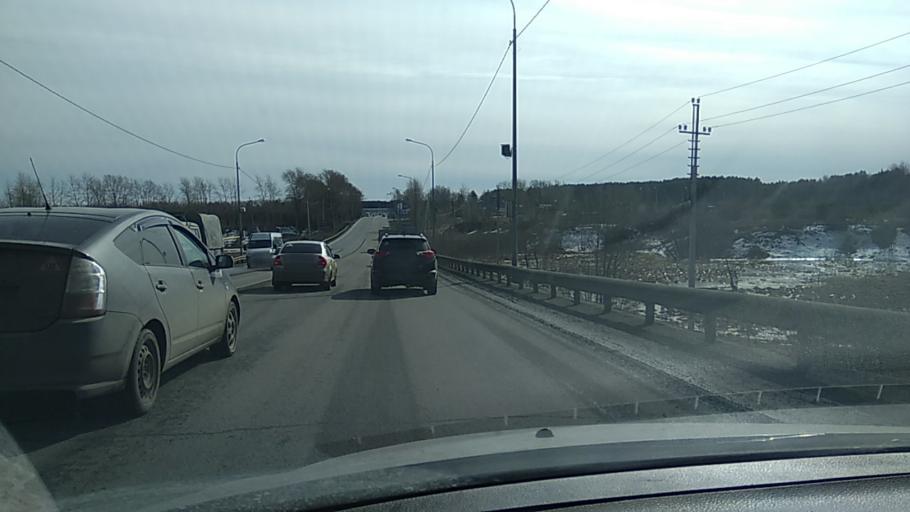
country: RU
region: Sverdlovsk
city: Nizhniy Tagil
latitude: 57.8847
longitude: 60.0168
